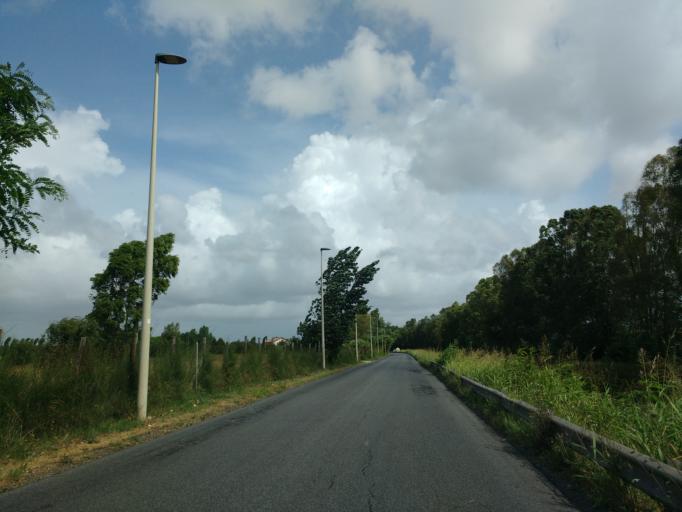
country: IT
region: Latium
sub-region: Citta metropolitana di Roma Capitale
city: Acilia-Castel Fusano-Ostia Antica
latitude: 41.7568
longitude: 12.3299
